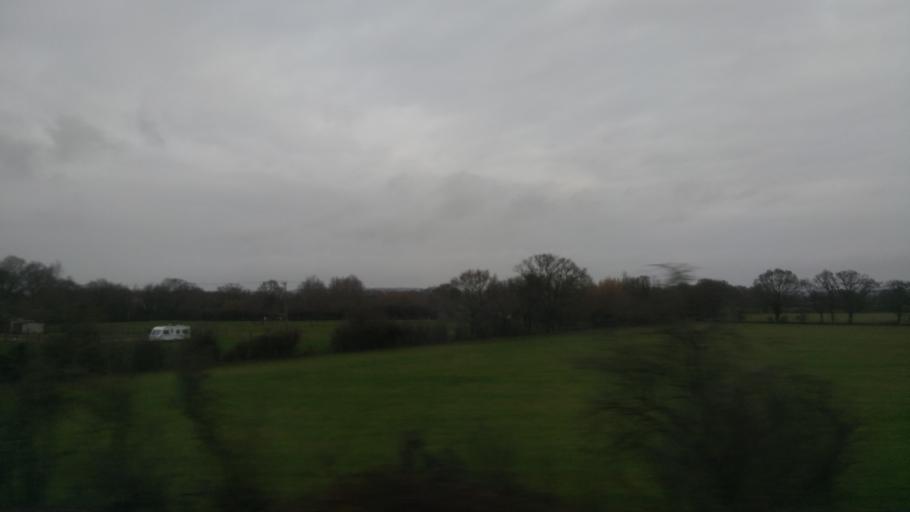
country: GB
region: England
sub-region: Kent
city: Headcorn
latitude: 51.1628
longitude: 0.6659
